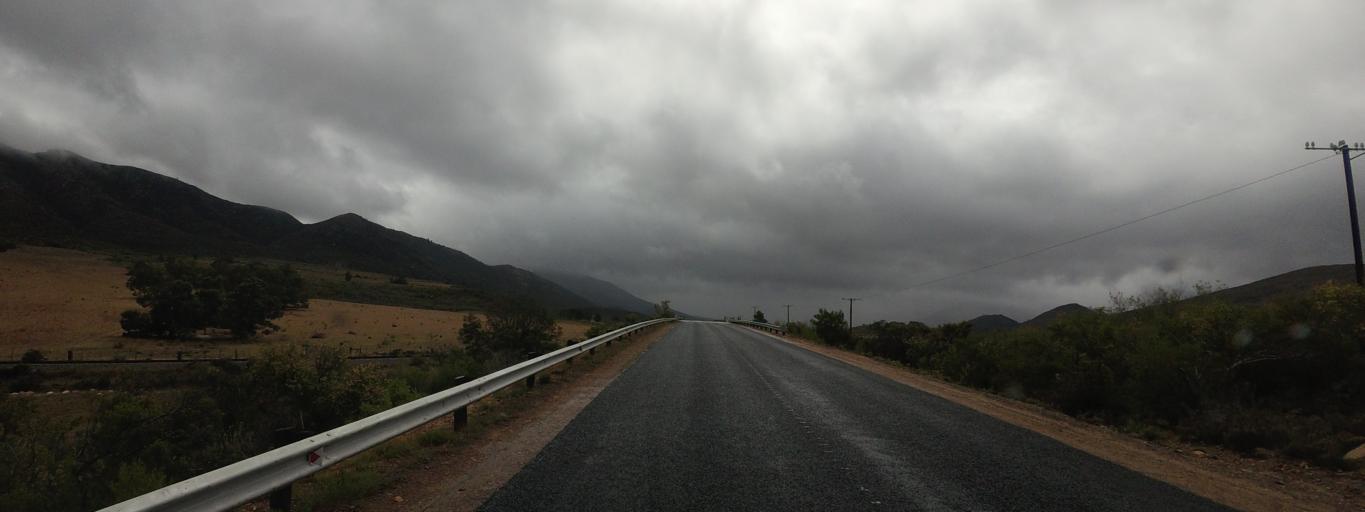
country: ZA
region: Western Cape
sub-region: Eden District Municipality
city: George
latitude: -33.8275
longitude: 22.4032
